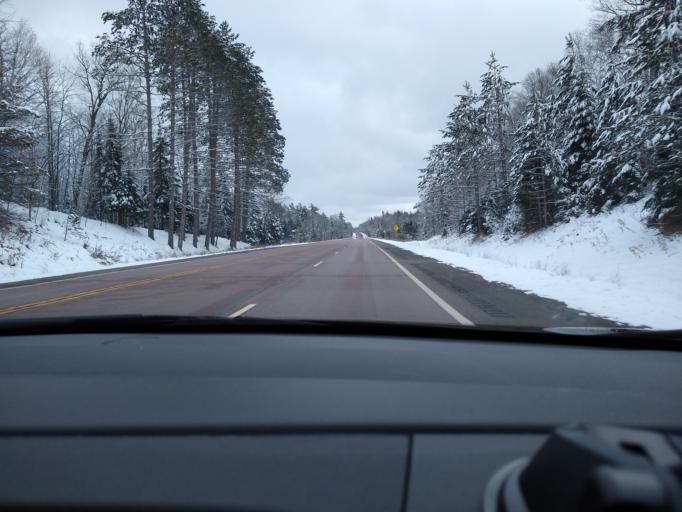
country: US
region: Michigan
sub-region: Iron County
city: Iron River
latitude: 46.1899
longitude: -88.9874
